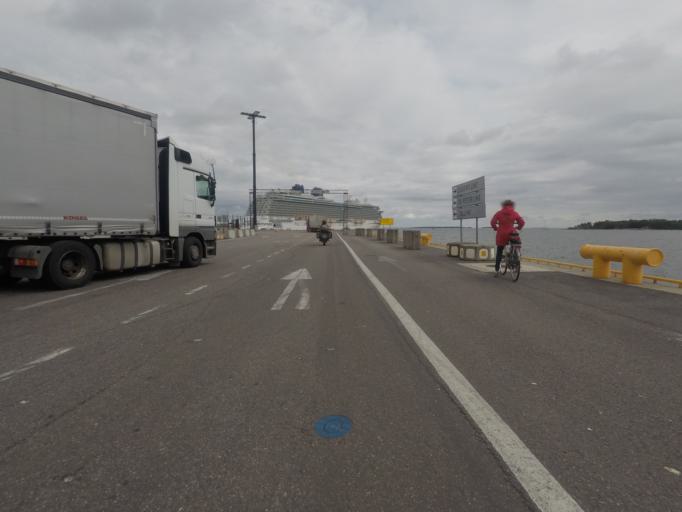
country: FI
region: Uusimaa
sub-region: Helsinki
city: Helsinki
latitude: 60.1477
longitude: 24.9124
